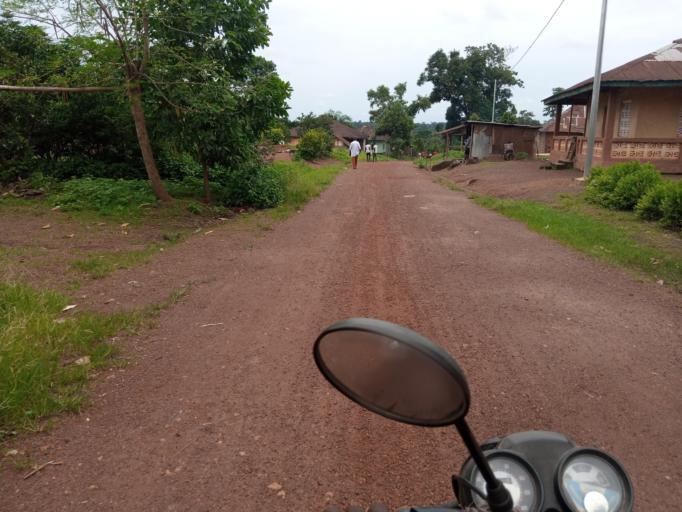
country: SL
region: Southern Province
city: Largo
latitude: 8.2016
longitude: -12.0600
